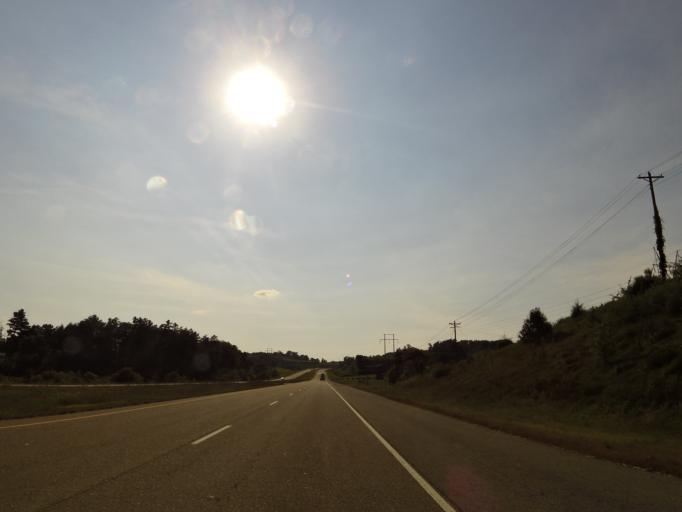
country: US
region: Tennessee
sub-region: Loudon County
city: Greenback
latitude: 35.7377
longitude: -84.1886
